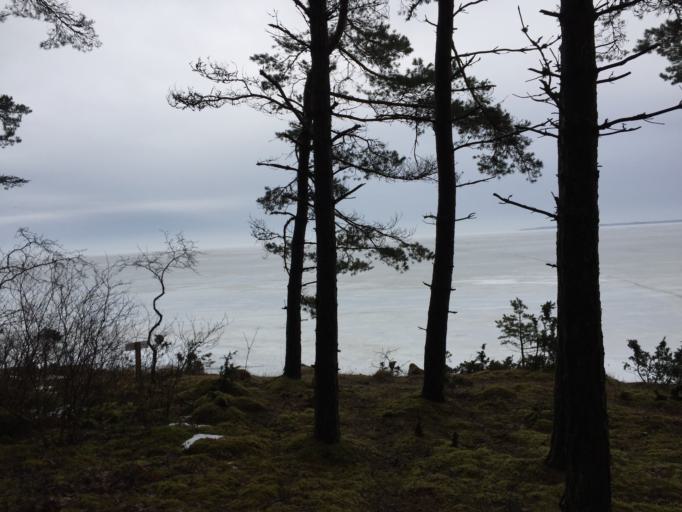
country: EE
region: Saare
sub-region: Orissaare vald
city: Orissaare
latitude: 58.6137
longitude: 22.9572
